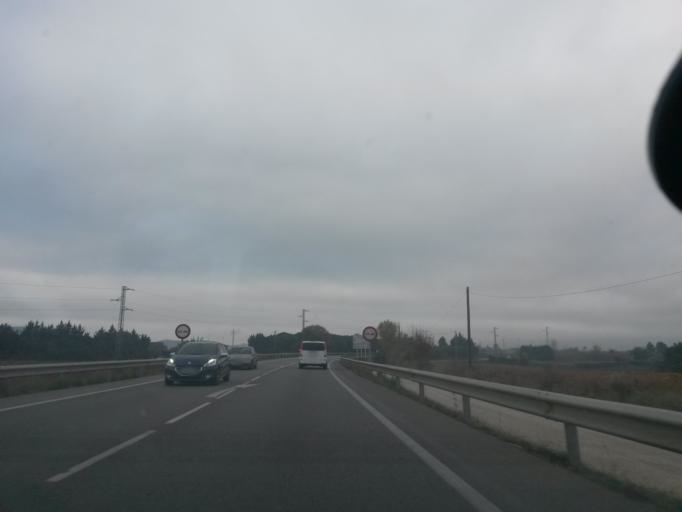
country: ES
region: Catalonia
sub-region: Provincia de Girona
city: Banyoles
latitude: 42.1287
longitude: 2.7763
